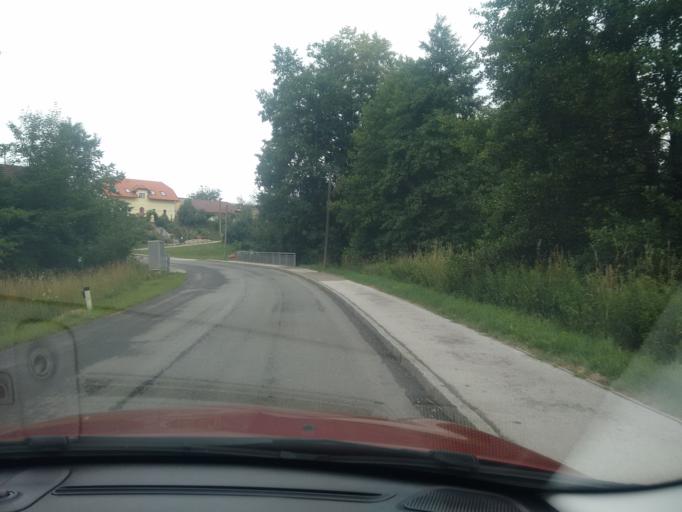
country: AT
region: Upper Austria
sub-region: Politischer Bezirk Steyr-Land
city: Bad Hall
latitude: 48.0403
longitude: 14.2211
